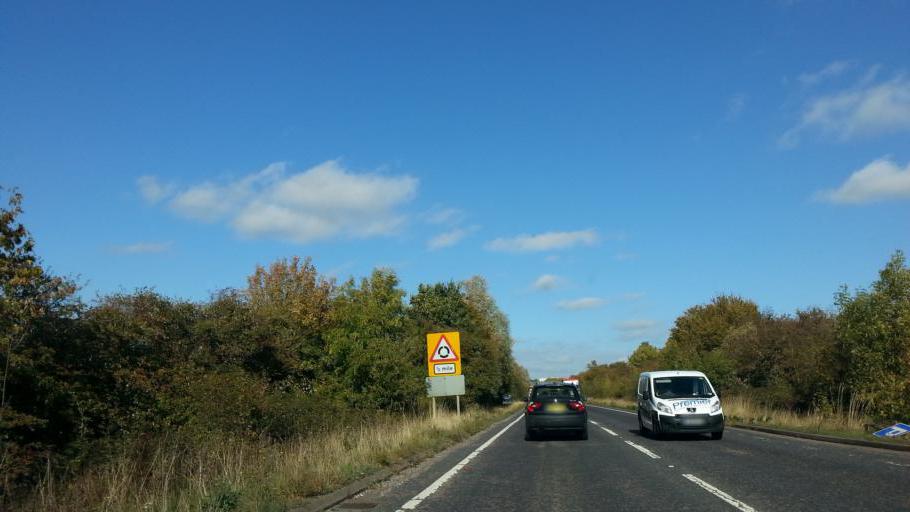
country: GB
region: England
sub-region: Northamptonshire
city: Thrapston
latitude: 52.3843
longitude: -0.5238
